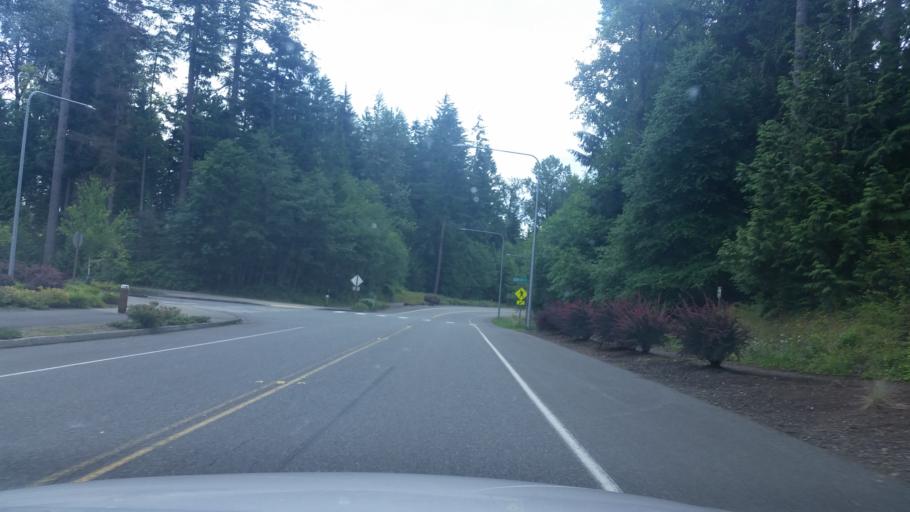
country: US
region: Washington
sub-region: King County
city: Union Hill-Novelty Hill
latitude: 47.7203
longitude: -122.0285
